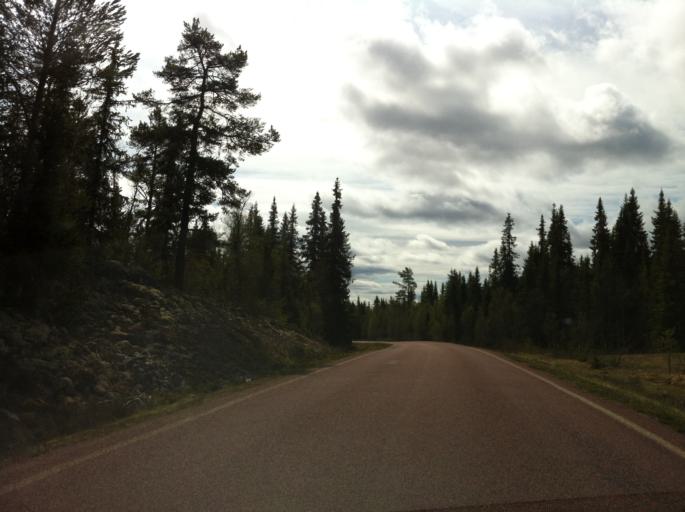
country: NO
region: Hedmark
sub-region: Engerdal
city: Engerdal
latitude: 62.1594
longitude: 12.9460
